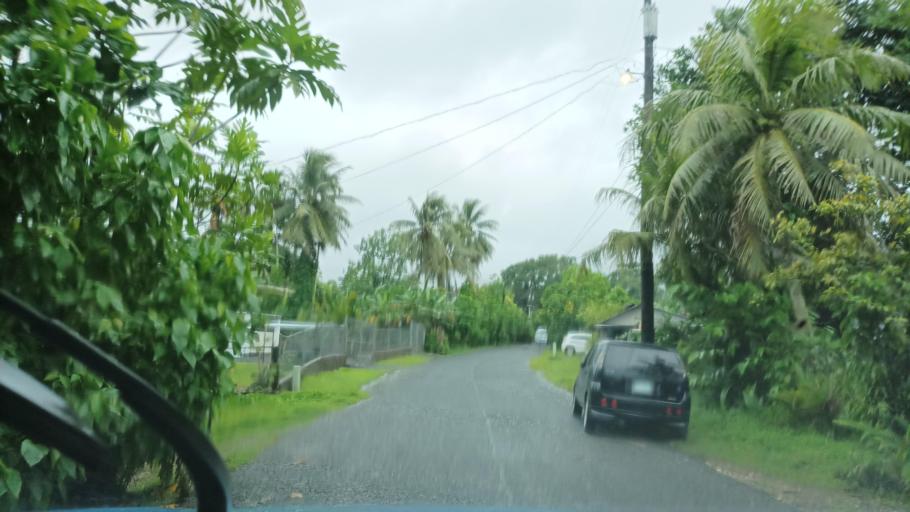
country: FM
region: Pohnpei
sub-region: Kolonia Municipality
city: Kolonia
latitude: 6.9698
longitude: 158.2075
